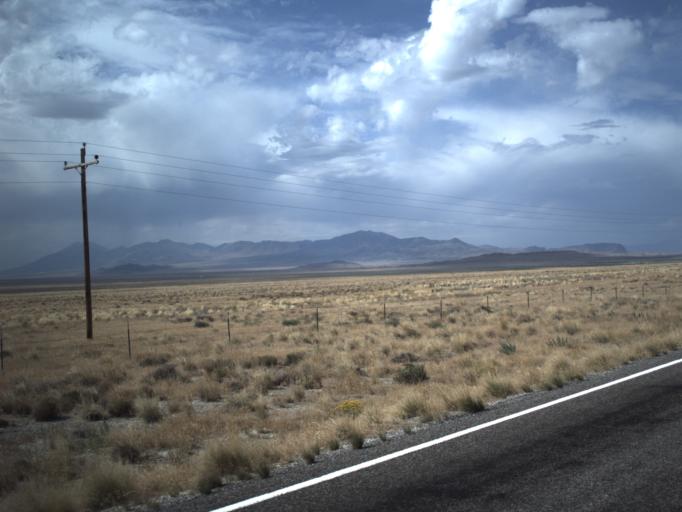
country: US
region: Utah
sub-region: Tooele County
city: Wendover
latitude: 41.4329
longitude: -113.7813
